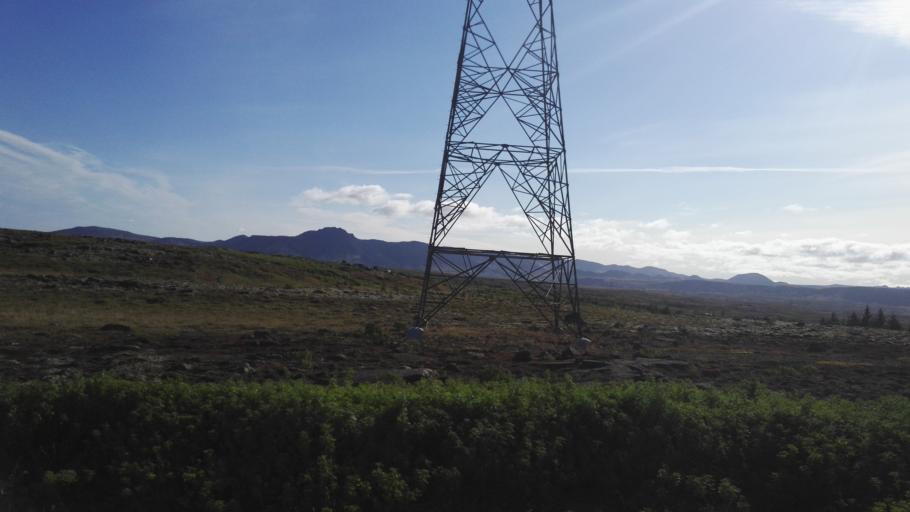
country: IS
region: Capital Region
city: Mosfellsbaer
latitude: 64.1067
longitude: -21.6121
